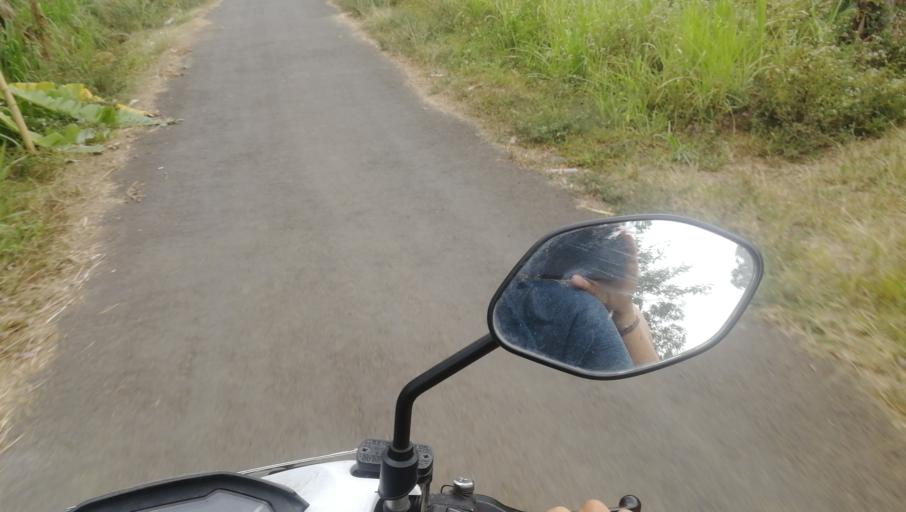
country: ID
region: Bali
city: Banjar Ambengan
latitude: -8.2115
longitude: 115.1106
